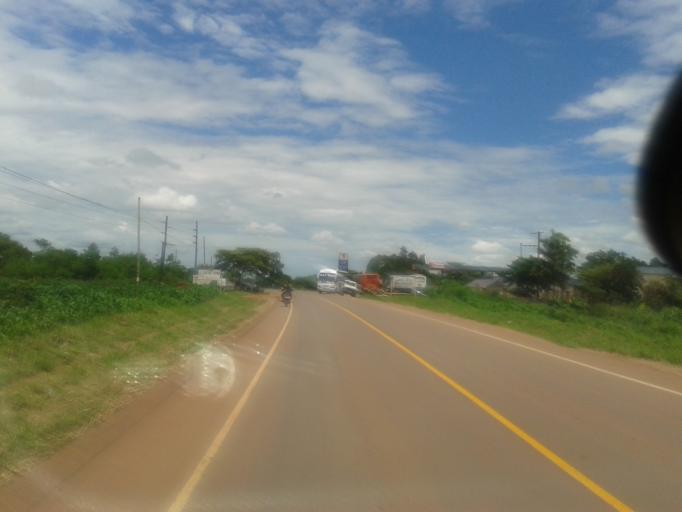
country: UG
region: Western Region
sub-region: Kiryandongo District
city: Kiryandongo
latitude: 1.8042
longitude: 32.0096
